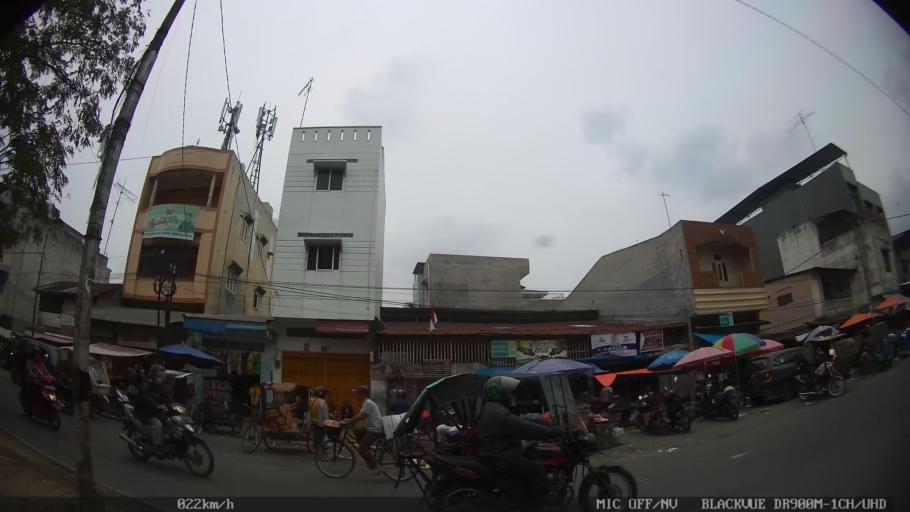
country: ID
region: North Sumatra
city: Medan
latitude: 3.5834
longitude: 98.7052
